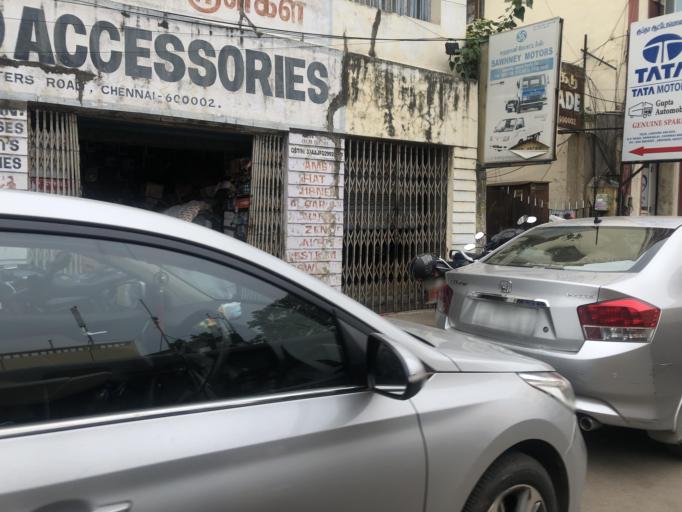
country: IN
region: Tamil Nadu
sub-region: Chennai
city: Chetput
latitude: 13.0626
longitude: 80.2670
